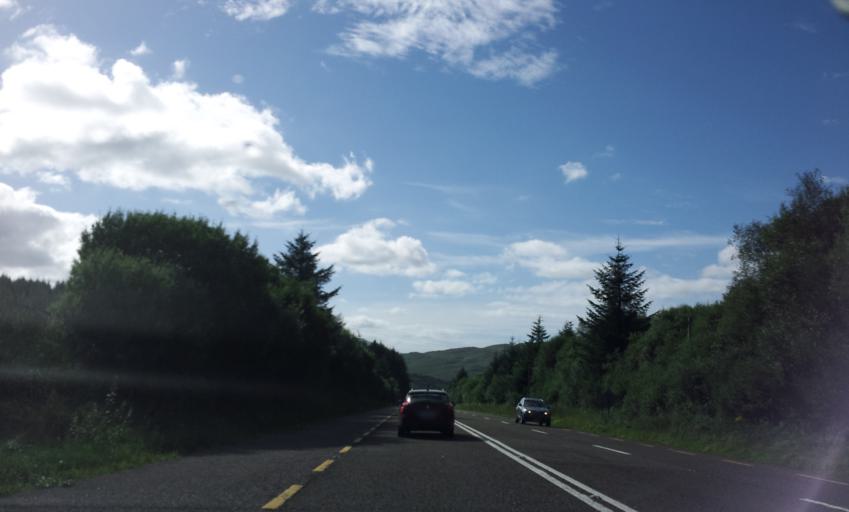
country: IE
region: Munster
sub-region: County Cork
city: Millstreet
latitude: 51.9806
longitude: -9.2597
